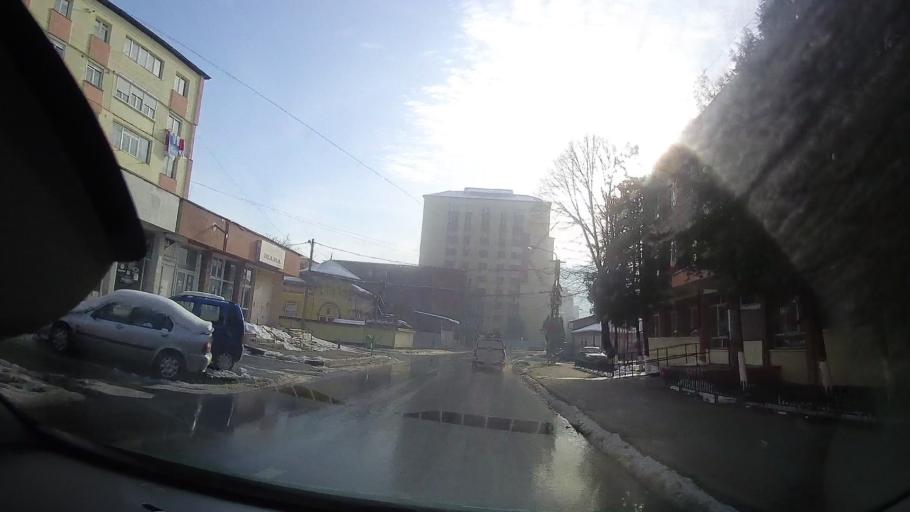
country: RO
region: Neamt
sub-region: Municipiul Piatra-Neamt
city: Valeni
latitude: 46.9409
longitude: 26.3820
